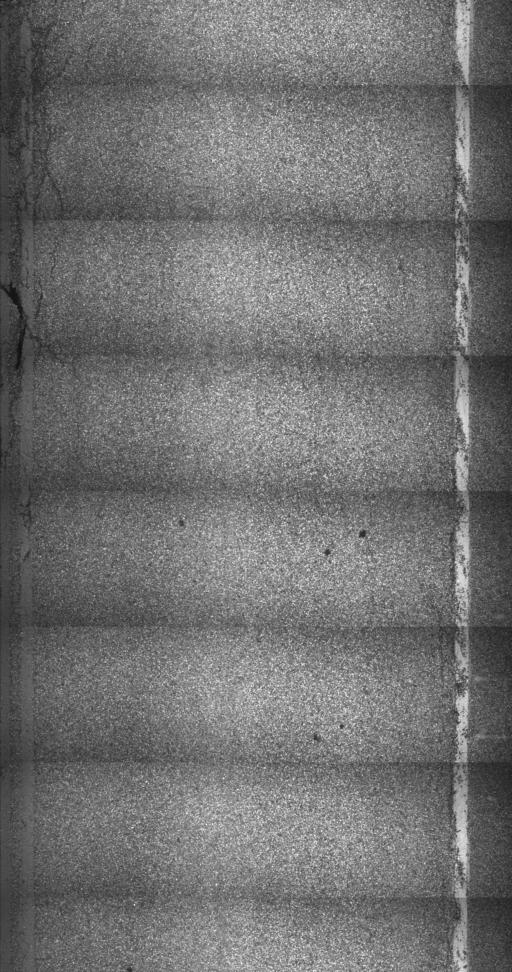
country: US
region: Vermont
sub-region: Rutland County
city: Rutland
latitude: 43.5708
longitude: -72.7624
